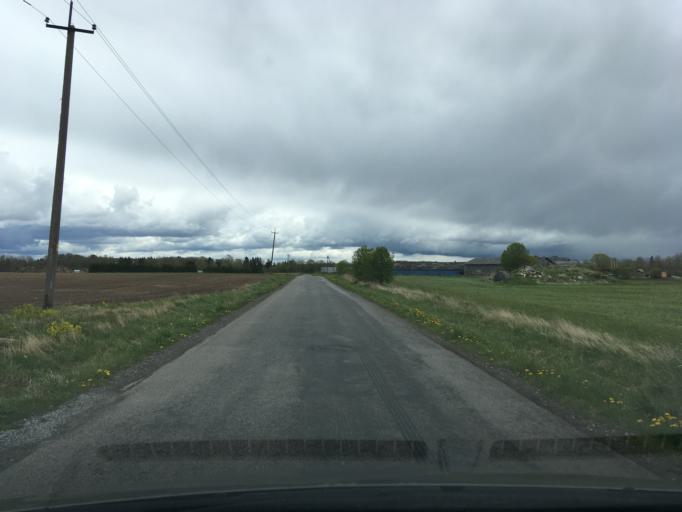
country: EE
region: Harju
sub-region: Rae vald
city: Jueri
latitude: 59.3676
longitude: 24.9626
